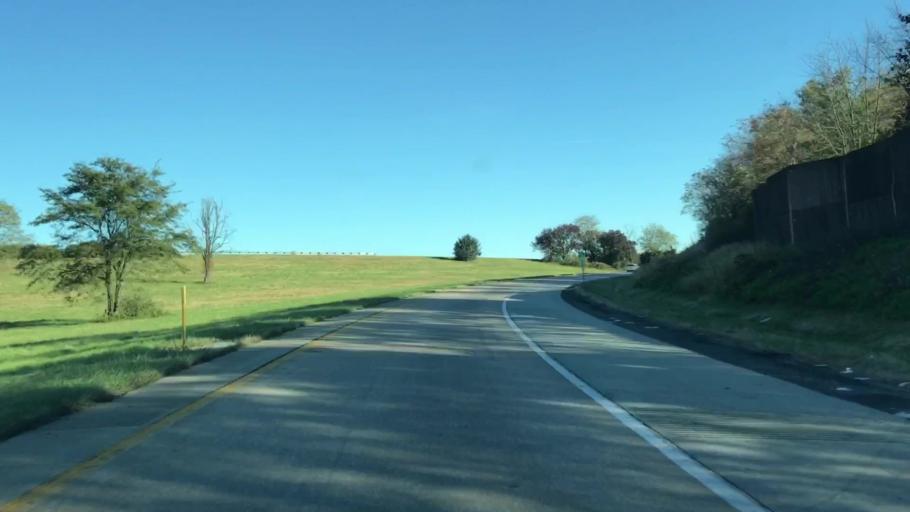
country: US
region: Pennsylvania
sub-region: Cumberland County
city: Mechanicsburg
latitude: 40.2736
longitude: -77.0038
